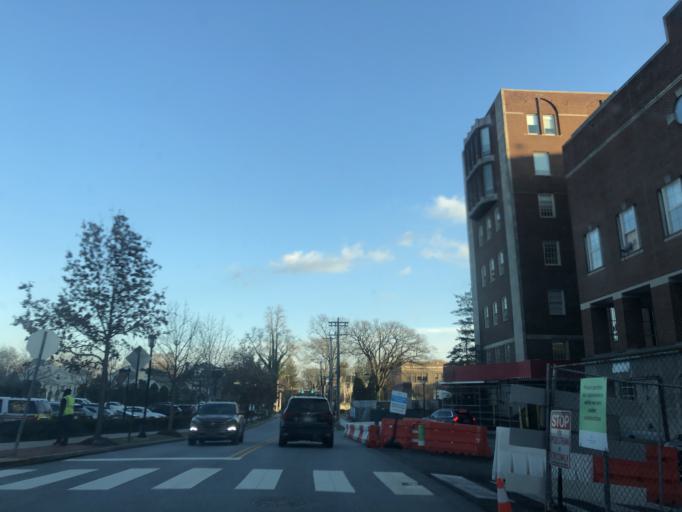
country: US
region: Pennsylvania
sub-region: Montgomery County
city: Bryn Mawr
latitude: 40.0200
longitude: -75.3212
